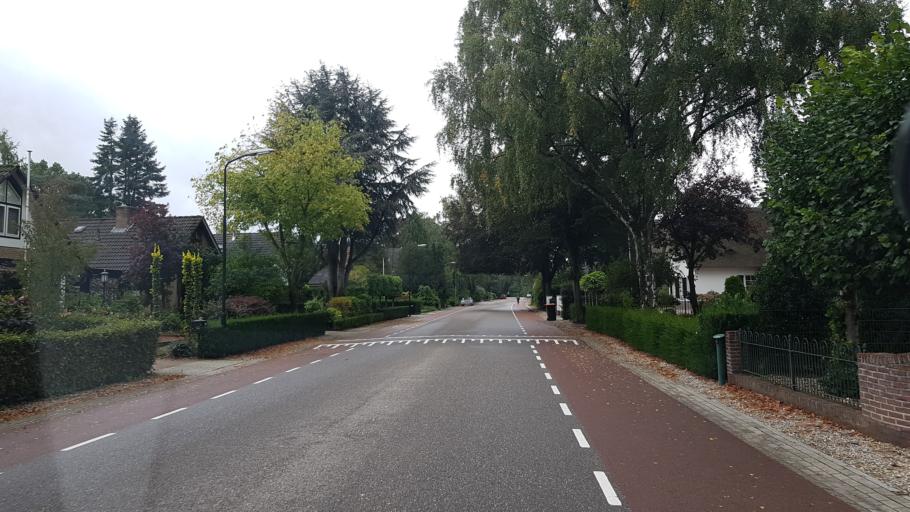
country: NL
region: Gelderland
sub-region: Gemeente Apeldoorn
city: Beekbergen
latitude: 52.1875
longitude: 5.9298
